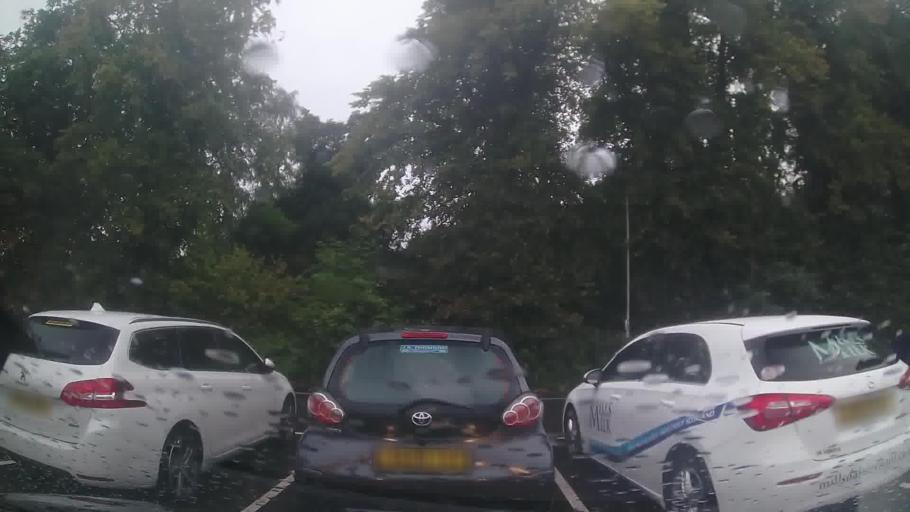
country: GB
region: Scotland
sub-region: East Ayrshire
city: Mauchline
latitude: 55.5155
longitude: -4.3821
